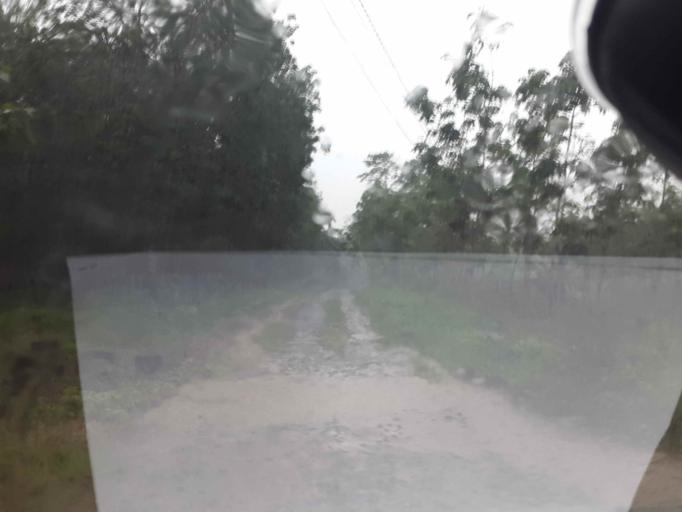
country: ID
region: Lampung
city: Kedaton
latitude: -5.3921
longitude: 105.3393
